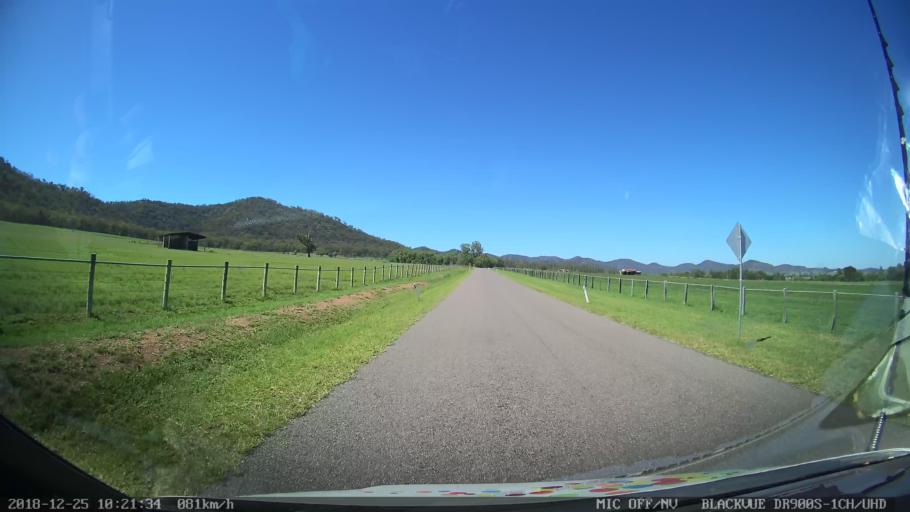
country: AU
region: New South Wales
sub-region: Muswellbrook
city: Denman
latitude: -32.3689
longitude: 150.5408
